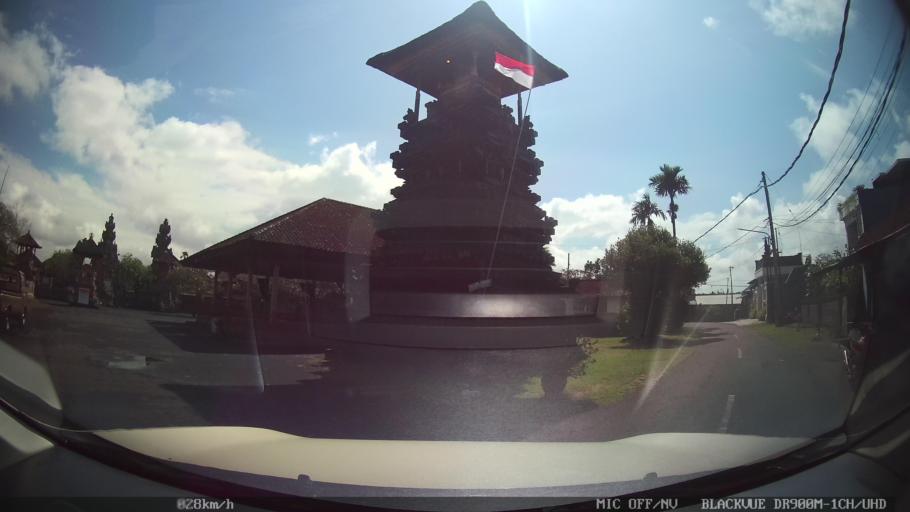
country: ID
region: Bali
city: Banjar Sedang
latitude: -8.5577
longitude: 115.2688
